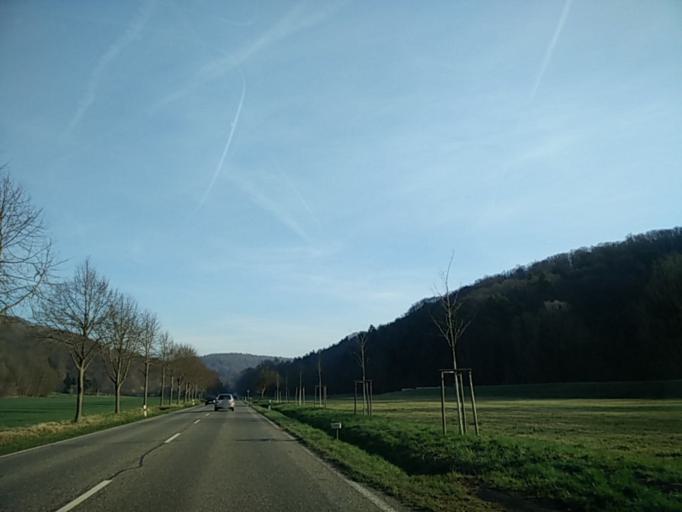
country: DE
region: Baden-Wuerttemberg
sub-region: Tuebingen Region
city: Tuebingen
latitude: 48.5368
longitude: 9.0769
